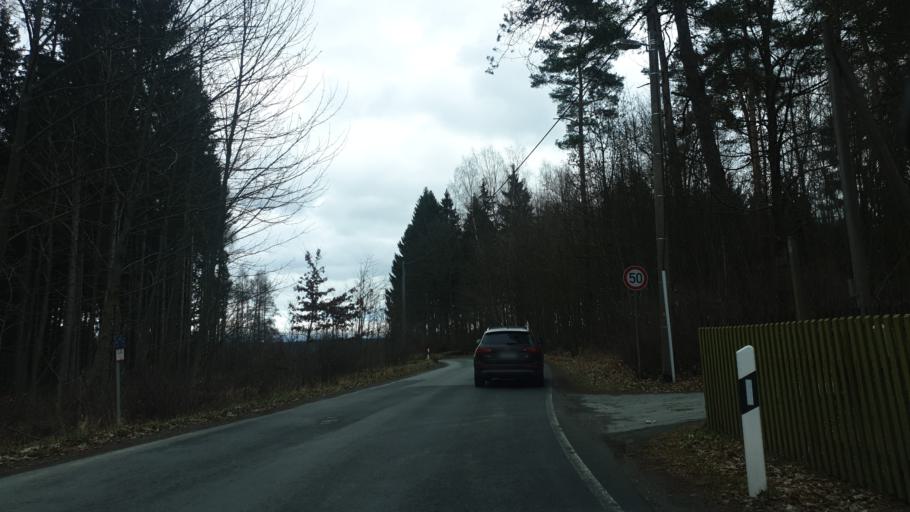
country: DE
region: Saxony
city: Bad Elster
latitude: 50.2744
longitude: 12.2724
